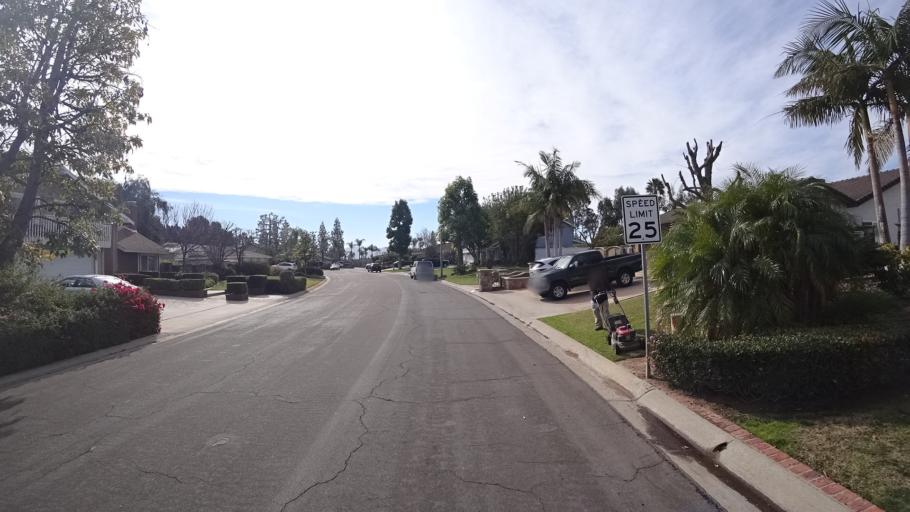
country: US
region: California
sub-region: Orange County
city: Yorba Linda
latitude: 33.8762
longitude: -117.7983
